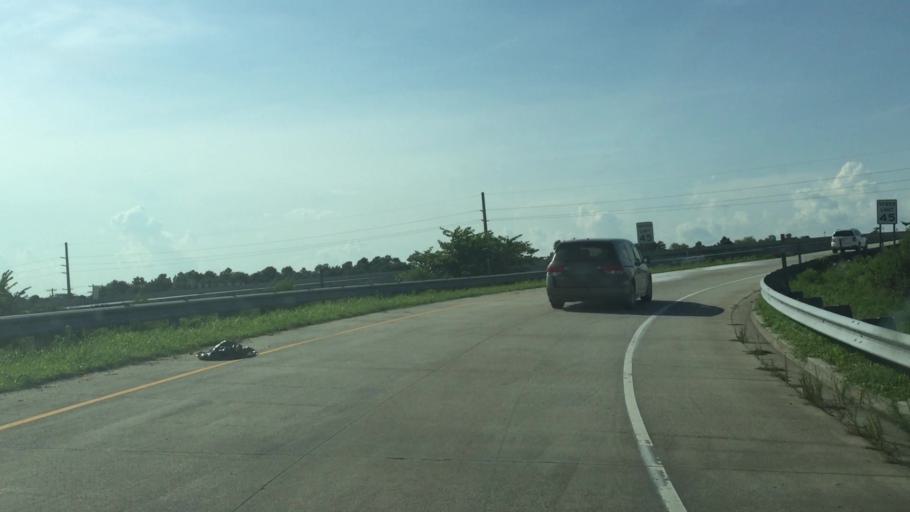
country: US
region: South Carolina
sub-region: Horry County
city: North Myrtle Beach
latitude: 33.7858
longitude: -78.7754
